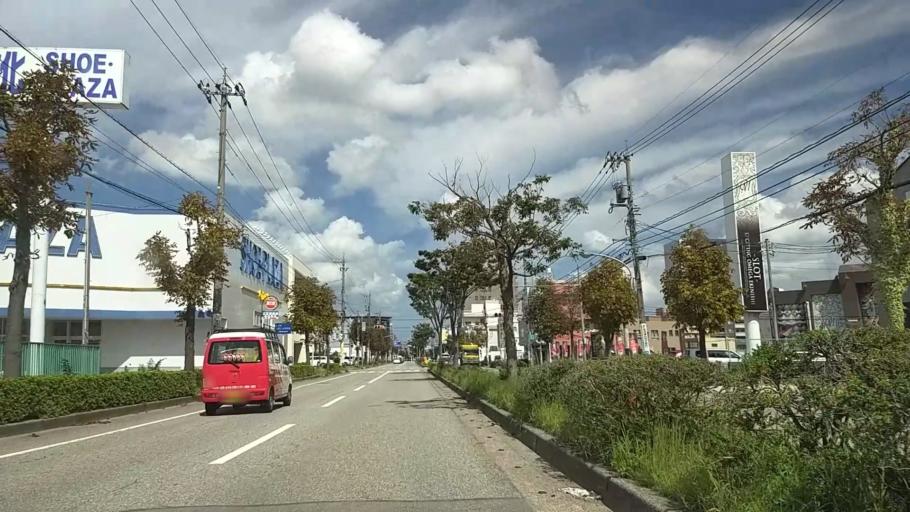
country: JP
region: Ishikawa
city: Kanazawa-shi
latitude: 36.5807
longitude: 136.6374
